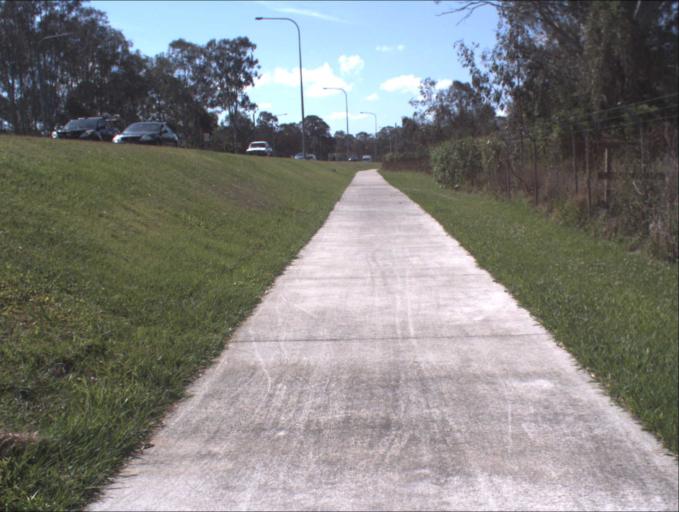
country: AU
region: Queensland
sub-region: Logan
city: Slacks Creek
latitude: -27.6517
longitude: 153.1453
